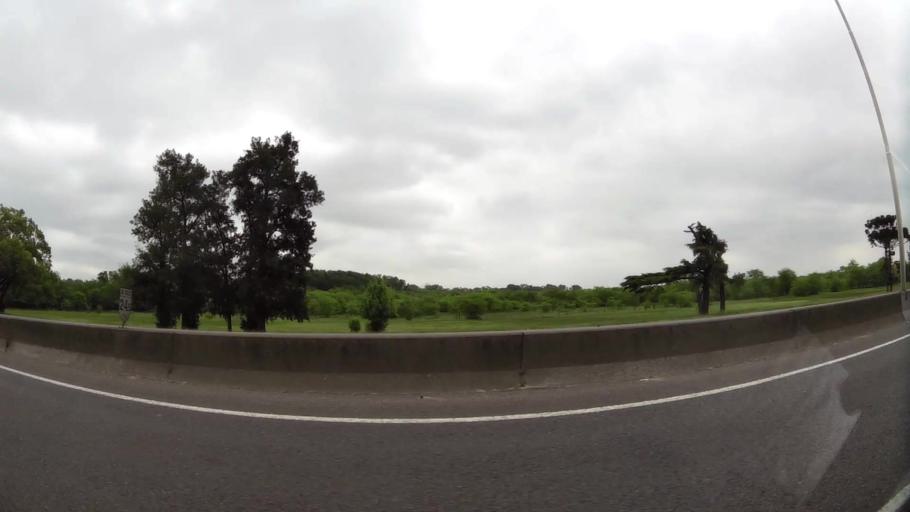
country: AR
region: Buenos Aires
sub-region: Partido de Ezeiza
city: Ezeiza
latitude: -34.7718
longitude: -58.5241
